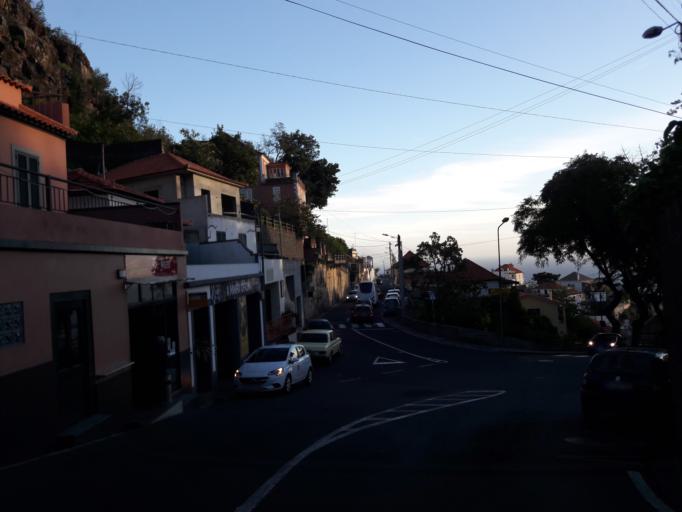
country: PT
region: Madeira
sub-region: Funchal
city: Nossa Senhora do Monte
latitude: 32.6610
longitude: -16.9023
